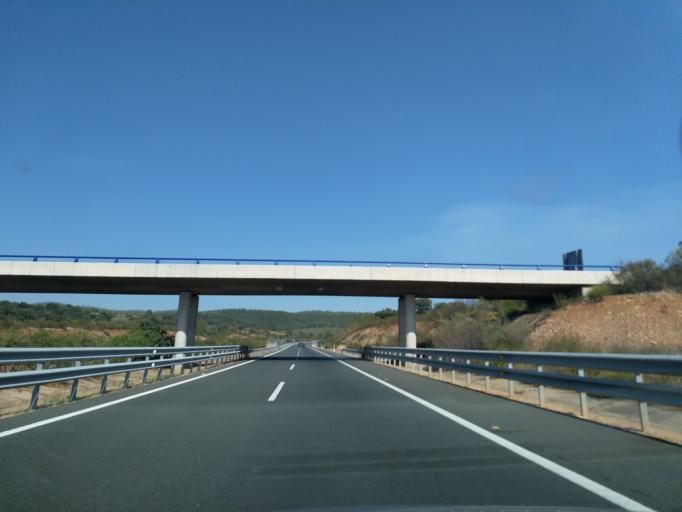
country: ES
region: Extremadura
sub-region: Provincia de Caceres
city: Alcuescar
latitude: 39.1446
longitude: -6.2741
